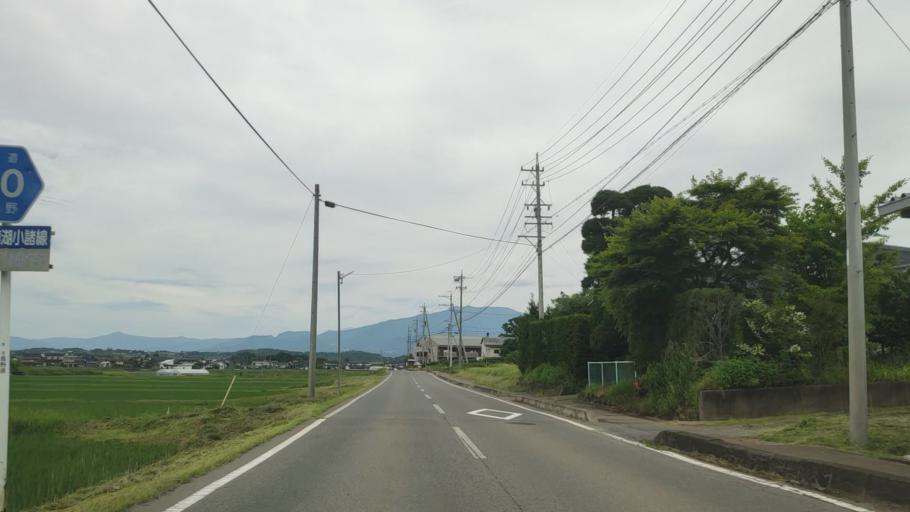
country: JP
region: Nagano
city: Kamimaruko
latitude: 36.2926
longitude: 138.3167
